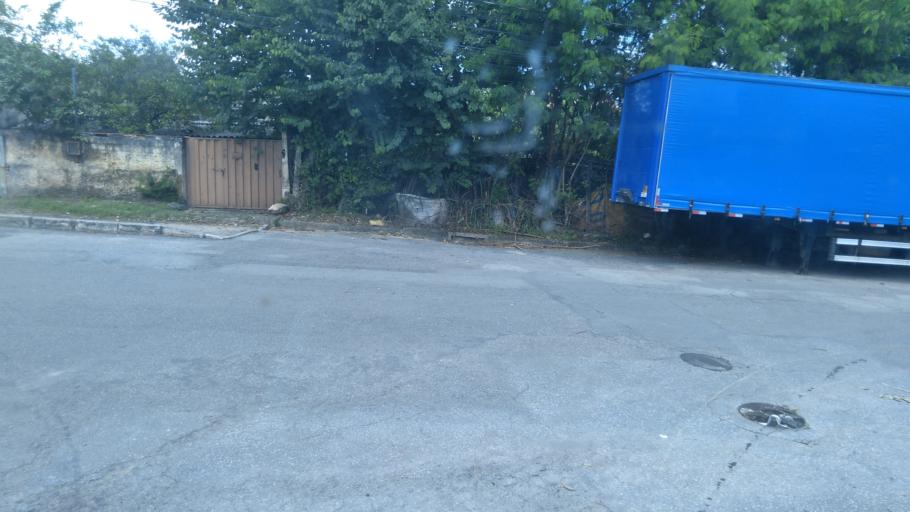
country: BR
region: Minas Gerais
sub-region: Belo Horizonte
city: Belo Horizonte
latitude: -19.8594
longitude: -43.8954
